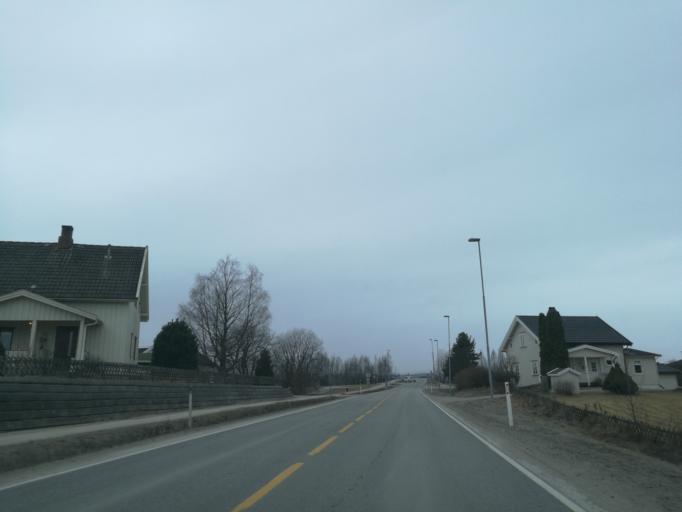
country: NO
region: Hedmark
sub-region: Grue
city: Kirkenaer
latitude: 60.4506
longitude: 12.0636
